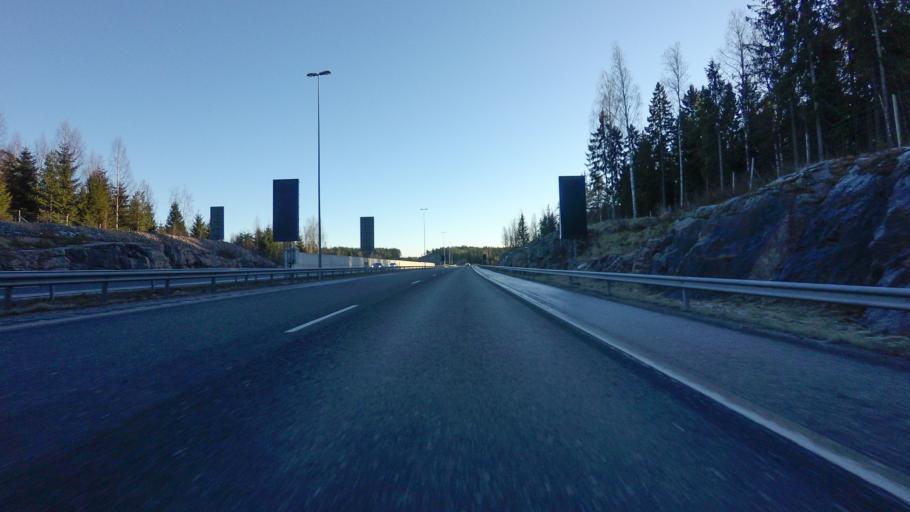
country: FI
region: Uusimaa
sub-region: Helsinki
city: Saukkola
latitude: 60.3200
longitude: 23.9653
